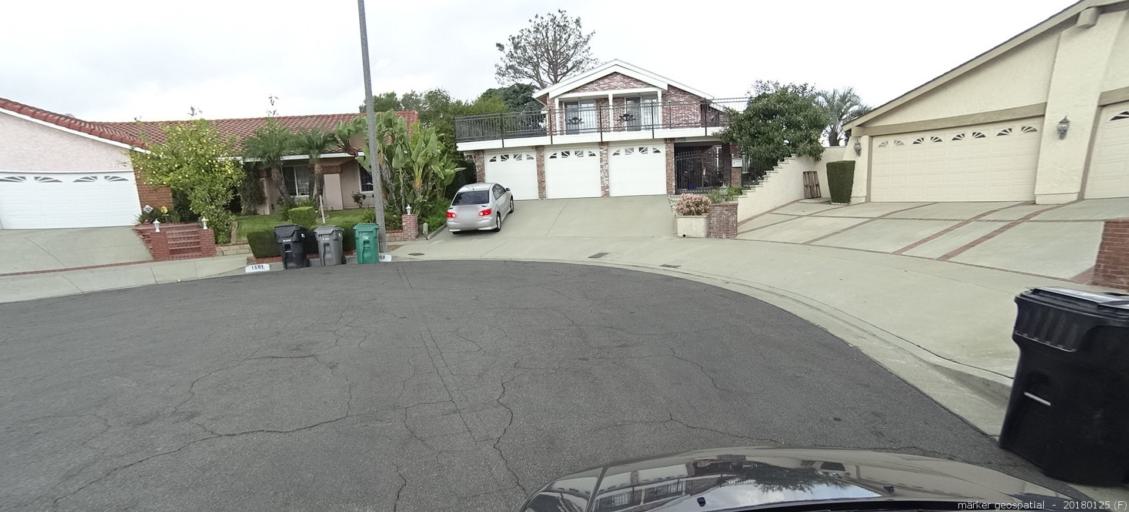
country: US
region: California
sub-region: Los Angeles County
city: Diamond Bar
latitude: 33.9926
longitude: -117.8267
